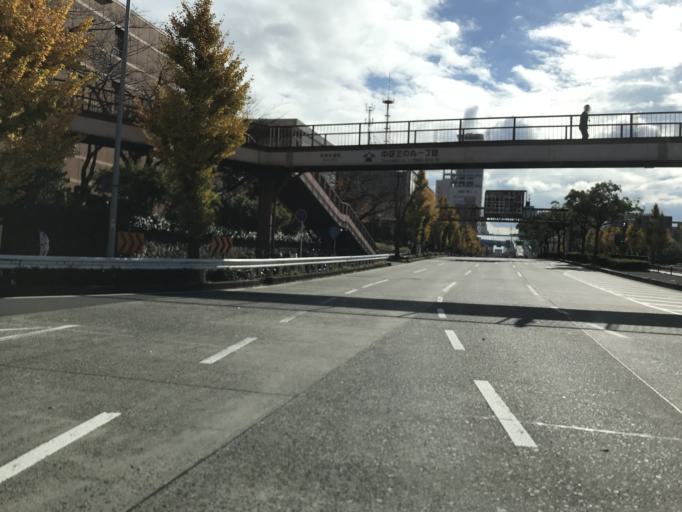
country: JP
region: Aichi
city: Nagoya-shi
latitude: 35.1810
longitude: 136.8963
